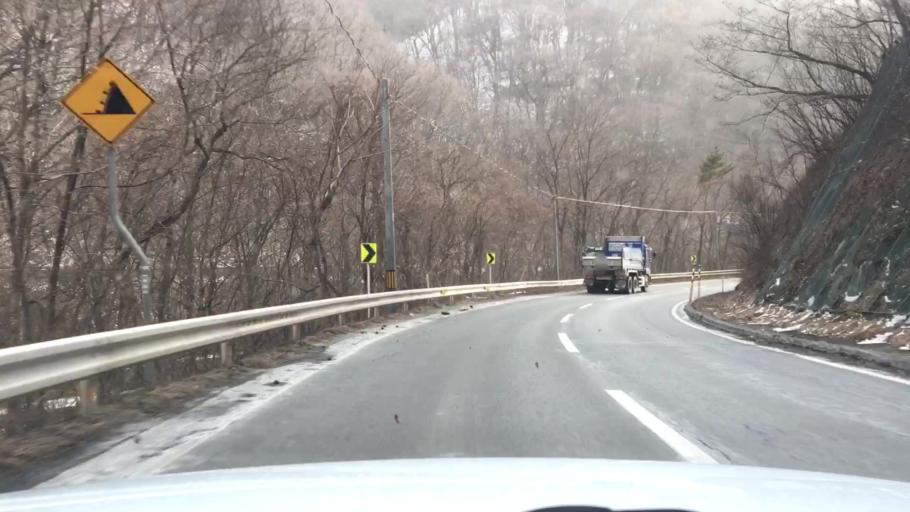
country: JP
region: Iwate
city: Tono
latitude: 39.6190
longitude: 141.5047
